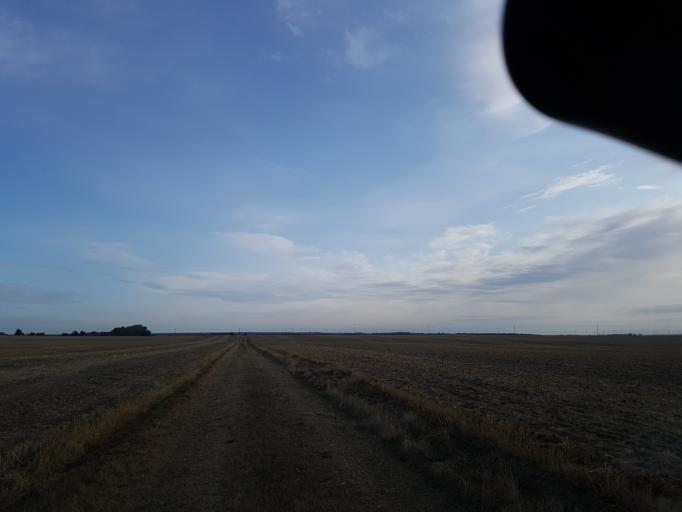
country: DE
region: Brandenburg
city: Niedergorsdorf
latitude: 51.9356
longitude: 13.0091
